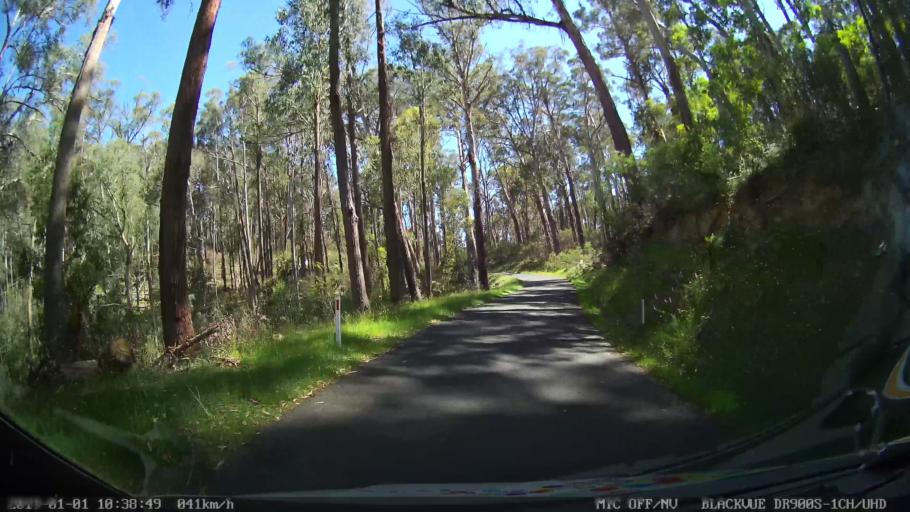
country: AU
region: New South Wales
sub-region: Snowy River
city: Jindabyne
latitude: -36.0432
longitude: 148.3012
